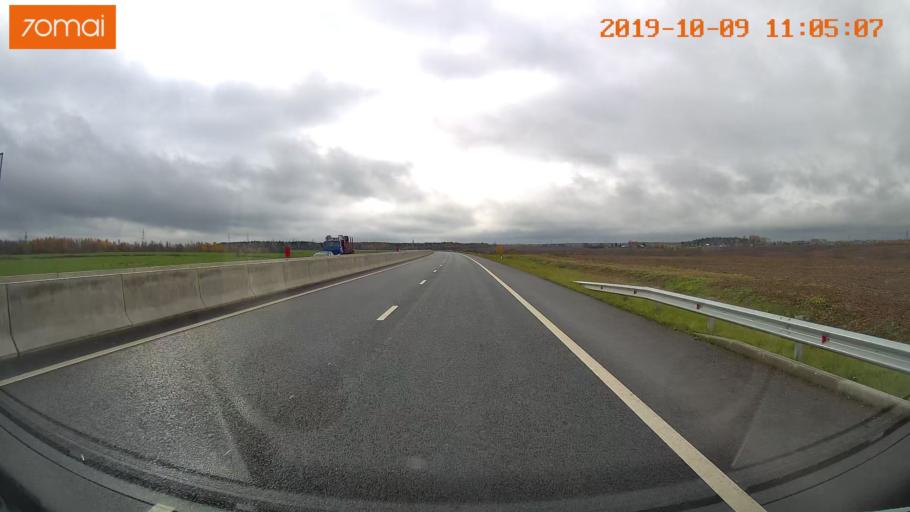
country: RU
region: Vologda
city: Molochnoye
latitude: 59.2040
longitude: 39.7598
